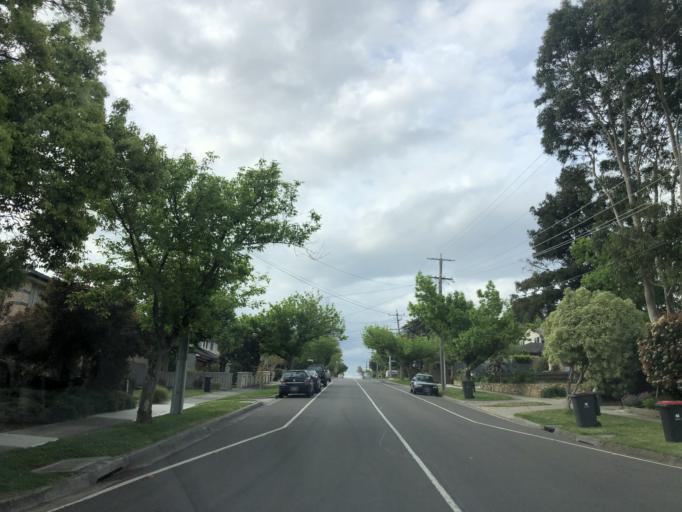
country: AU
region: Victoria
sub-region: Monash
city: Ashwood
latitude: -37.8664
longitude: 145.1189
